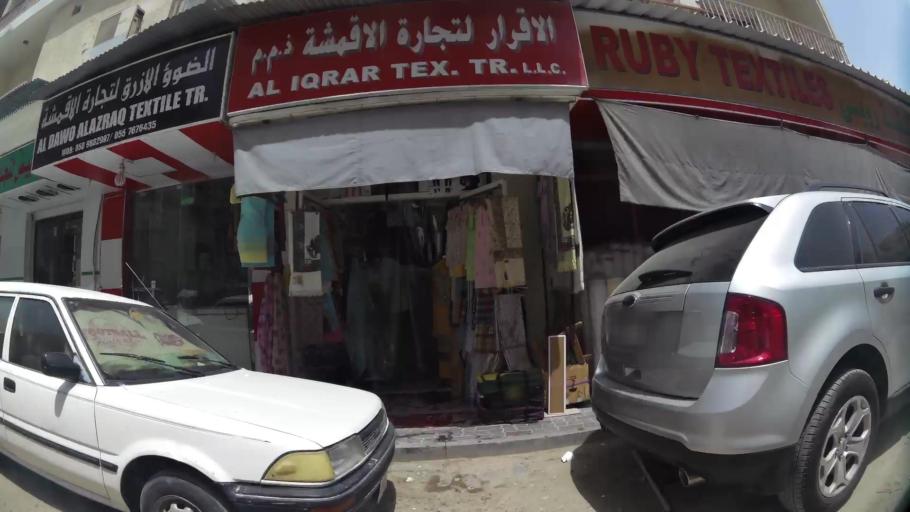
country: AE
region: Ash Shariqah
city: Sharjah
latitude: 25.3592
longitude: 55.3908
